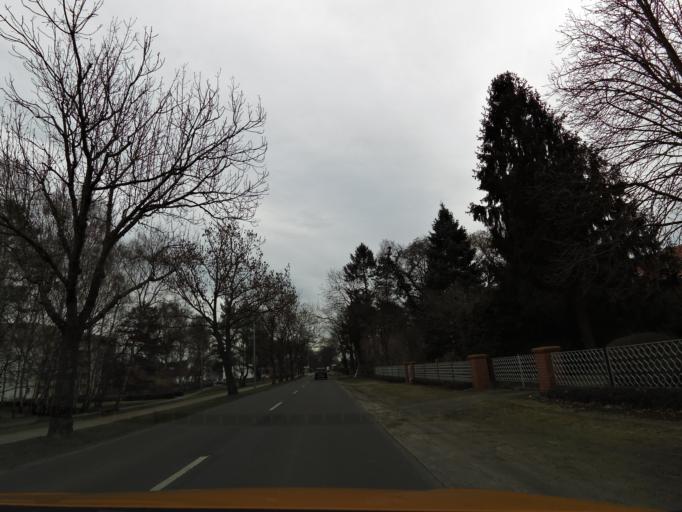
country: DE
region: Brandenburg
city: Belzig
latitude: 52.1387
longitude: 12.6022
